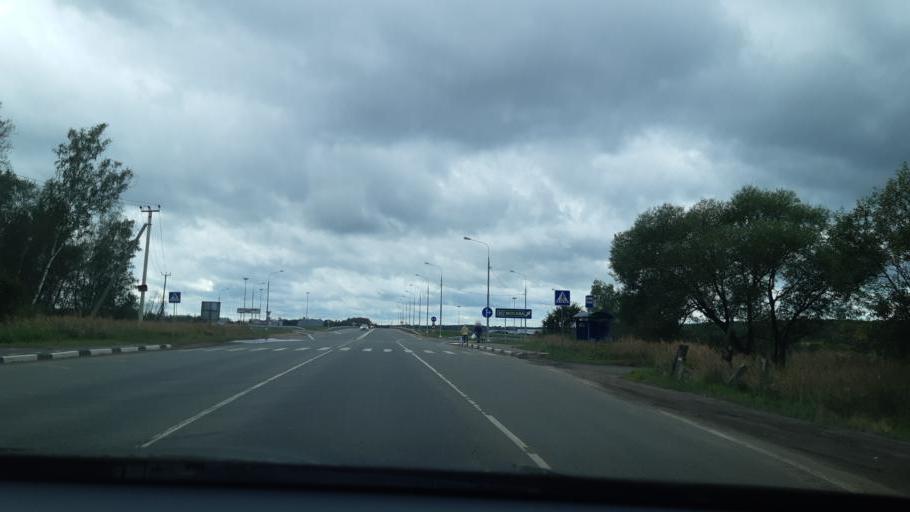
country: RU
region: Moskovskaya
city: Melikhovo
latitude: 55.1323
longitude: 37.5737
